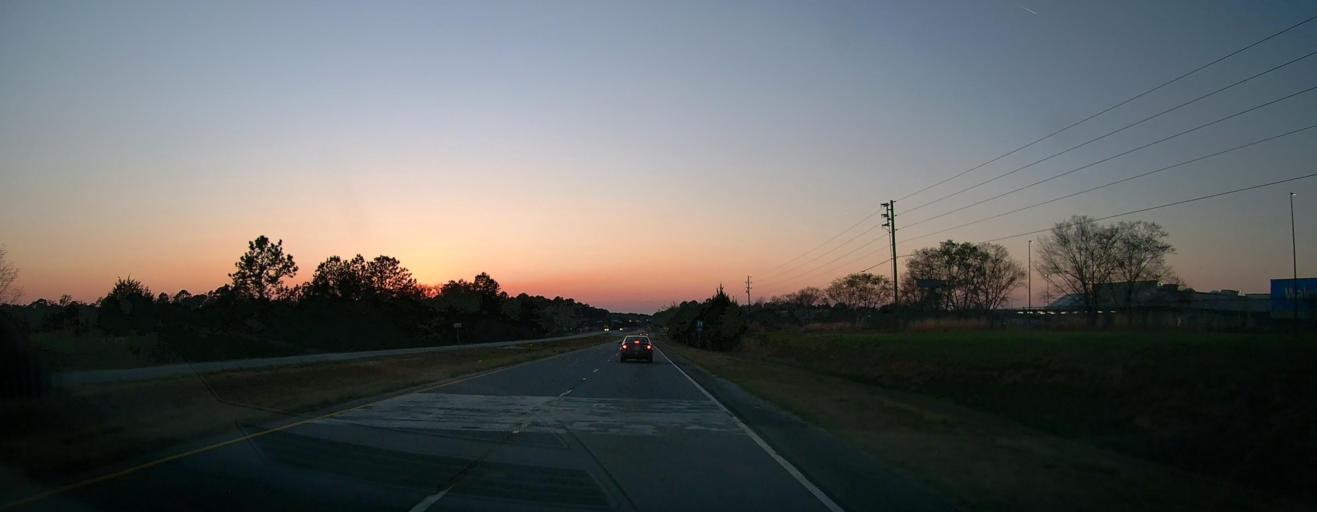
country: US
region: Georgia
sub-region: Dodge County
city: Eastman
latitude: 32.1773
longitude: -83.1772
